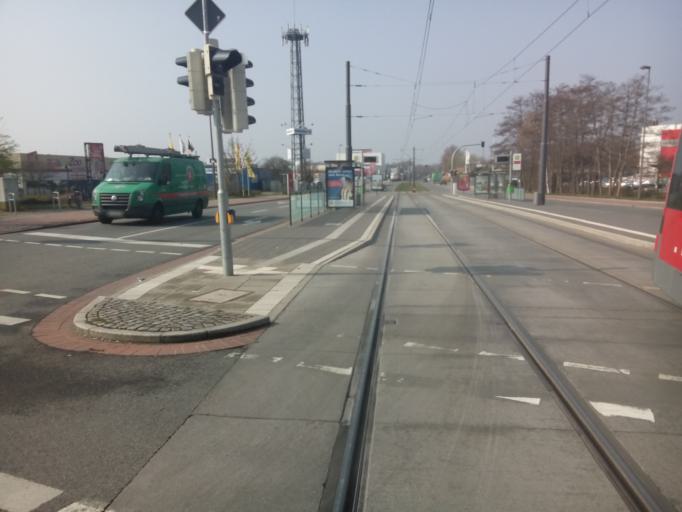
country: DE
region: Lower Saxony
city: Oyten
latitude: 53.0461
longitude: 8.9579
